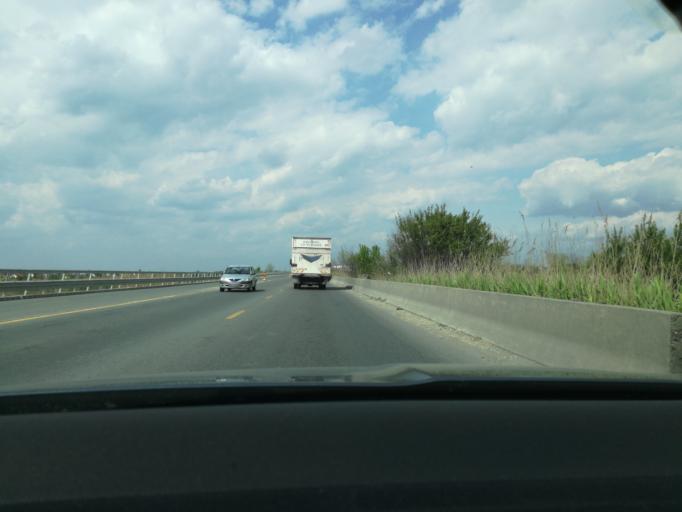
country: RO
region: Ilfov
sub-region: Comuna Dragomiresti-Vale
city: Dragomiresti-Deal
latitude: 44.4624
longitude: 25.9537
